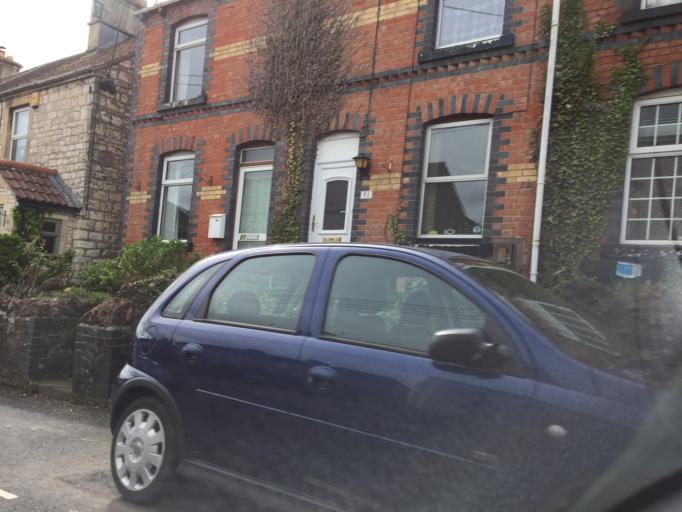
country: GB
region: England
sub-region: Bath and North East Somerset
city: Midsomer Norton
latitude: 51.2836
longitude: -2.4901
